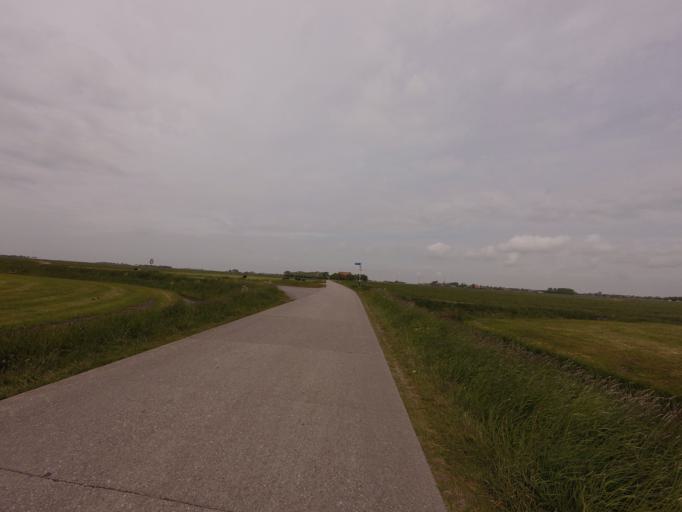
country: NL
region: Friesland
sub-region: Sudwest Fryslan
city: Makkum
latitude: 53.0672
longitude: 5.4576
